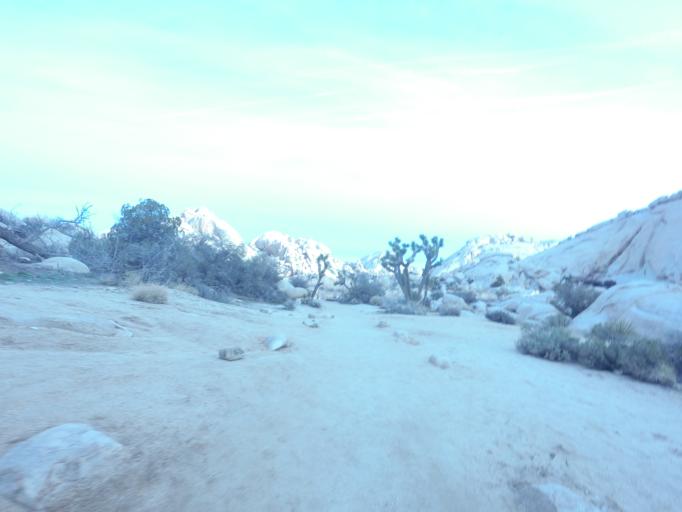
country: US
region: California
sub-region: San Bernardino County
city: Twentynine Palms
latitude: 34.0300
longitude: -116.1445
